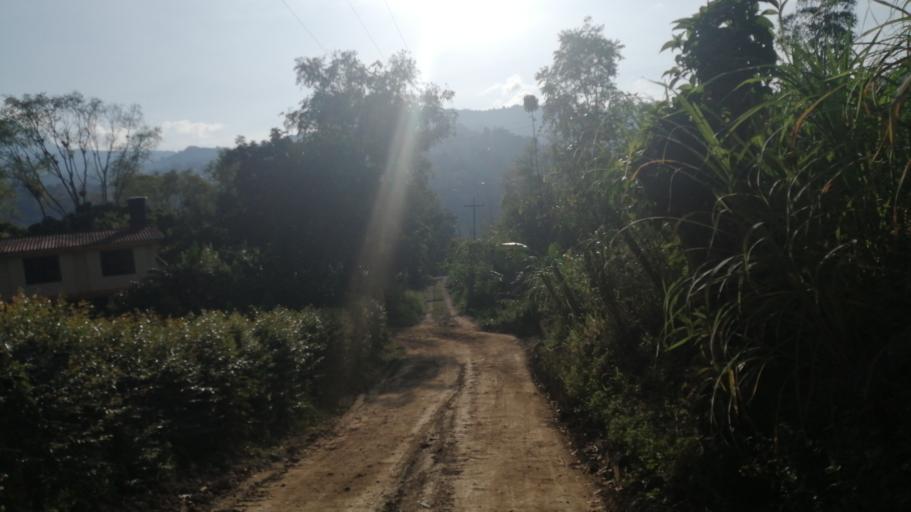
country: CO
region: Boyaca
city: Garagoa
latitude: 5.0800
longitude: -73.3900
